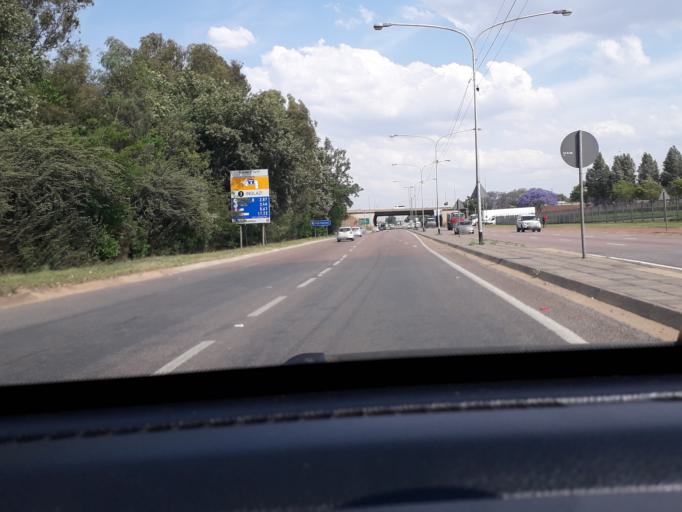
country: ZA
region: Gauteng
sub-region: City of Tshwane Metropolitan Municipality
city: Centurion
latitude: -25.8563
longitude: 28.2191
